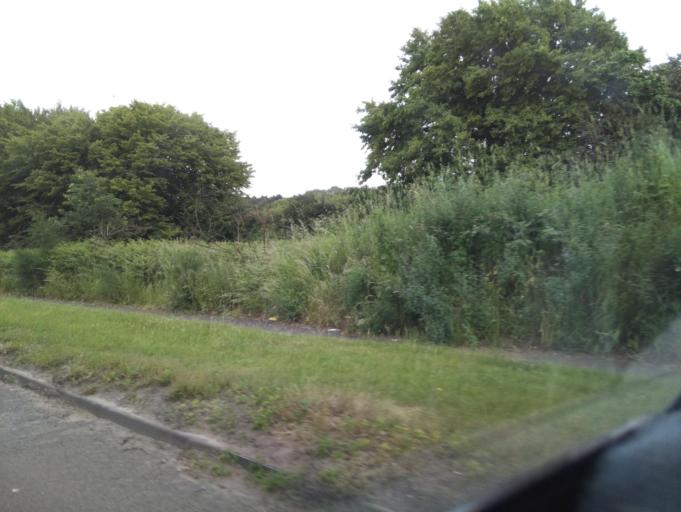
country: GB
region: England
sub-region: Dudley
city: Kingswinford
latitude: 52.4555
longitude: -2.2060
